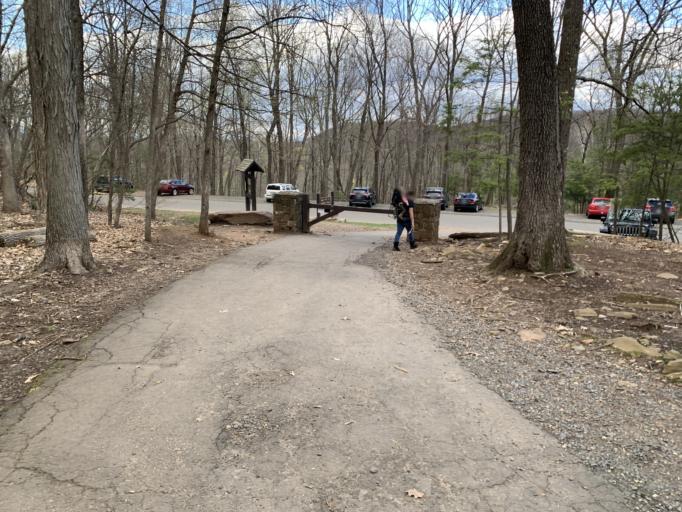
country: US
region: Connecticut
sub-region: Hartford County
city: Weatogue
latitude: 41.8393
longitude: -72.7926
